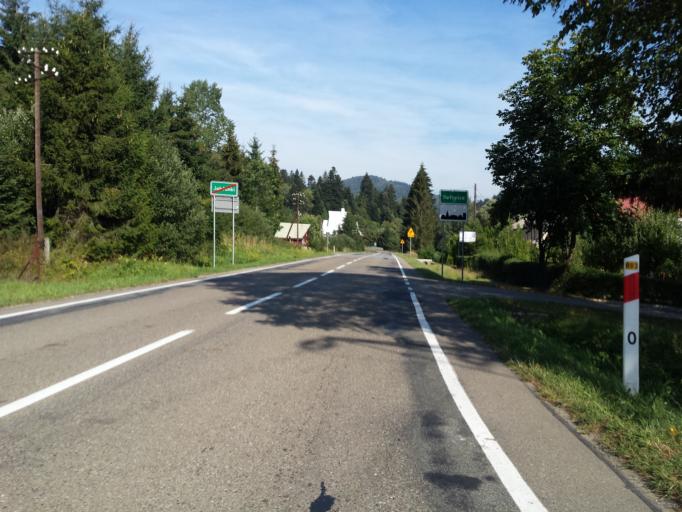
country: PL
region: Subcarpathian Voivodeship
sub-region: Powiat leski
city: Baligrod
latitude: 49.2797
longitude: 22.2810
